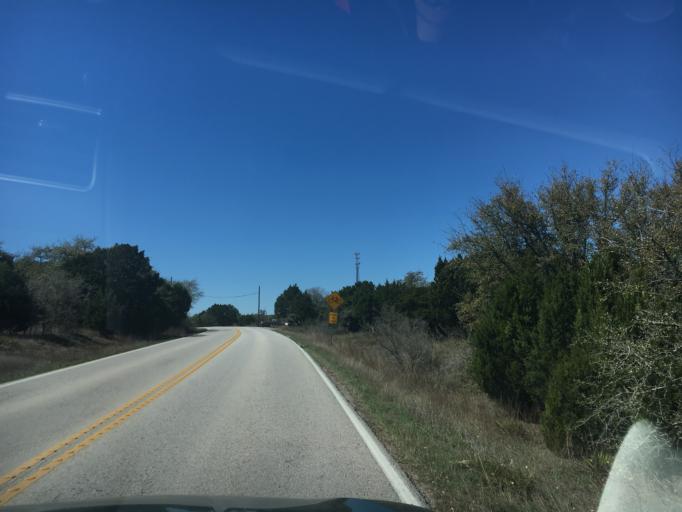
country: US
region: Texas
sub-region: Hays County
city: Dripping Springs
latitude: 30.2905
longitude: -98.0730
